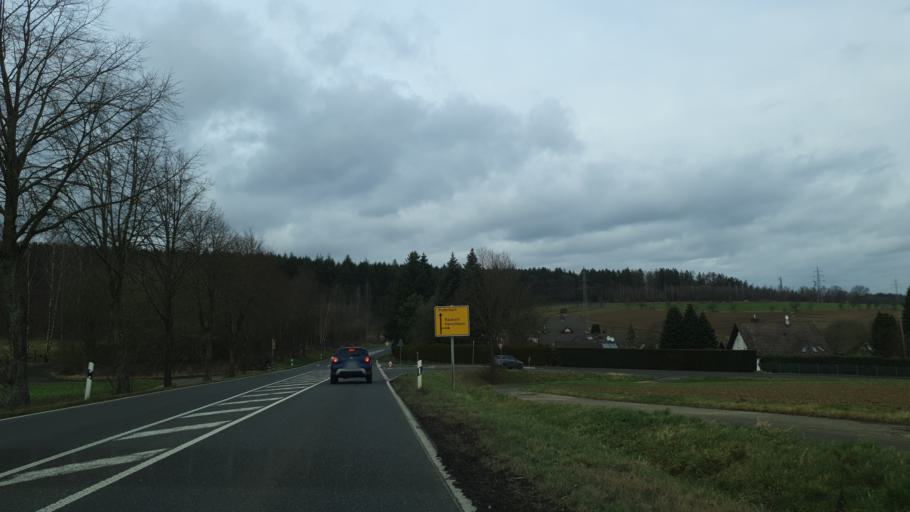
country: DE
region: Rheinland-Pfalz
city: Niederhofen
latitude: 50.5727
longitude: 7.5885
